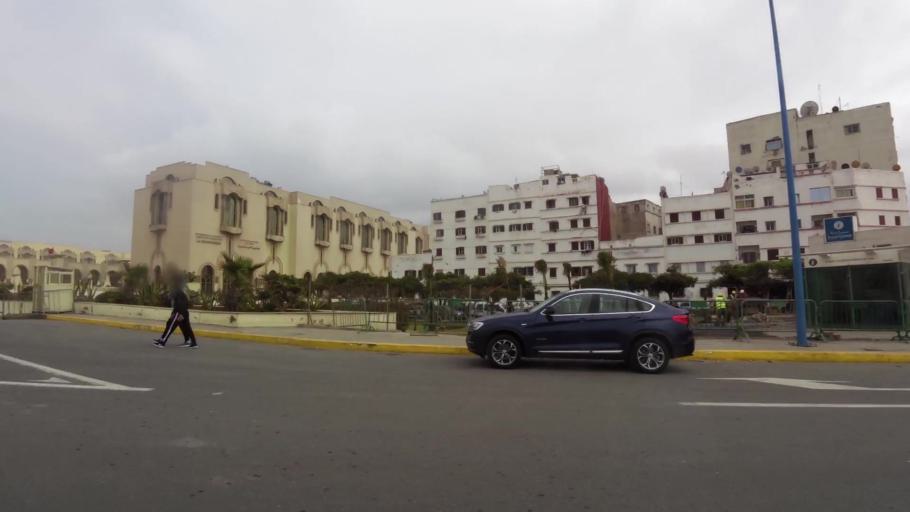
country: MA
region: Grand Casablanca
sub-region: Casablanca
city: Casablanca
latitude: 33.6060
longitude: -7.6336
